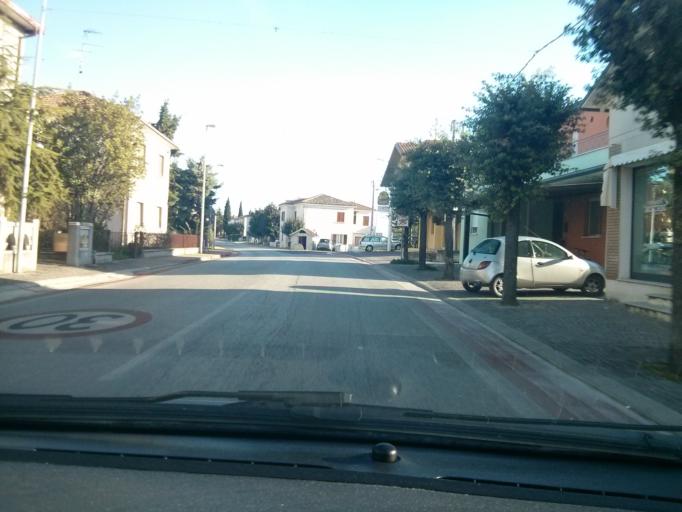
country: IT
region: The Marches
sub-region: Provincia di Pesaro e Urbino
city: Piagge
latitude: 43.7344
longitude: 12.9691
